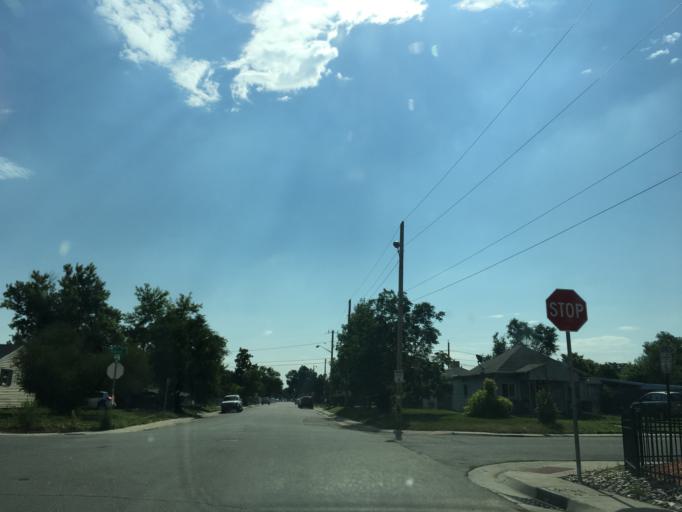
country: US
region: Colorado
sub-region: Jefferson County
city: Lakewood
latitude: 39.7022
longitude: -105.0427
